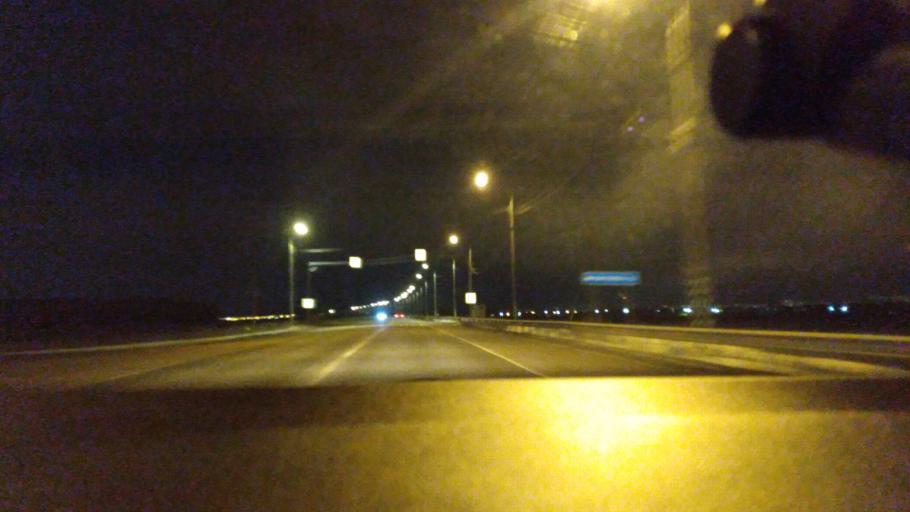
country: RU
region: Moskovskaya
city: Yegor'yevsk
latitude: 55.4034
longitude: 39.0575
